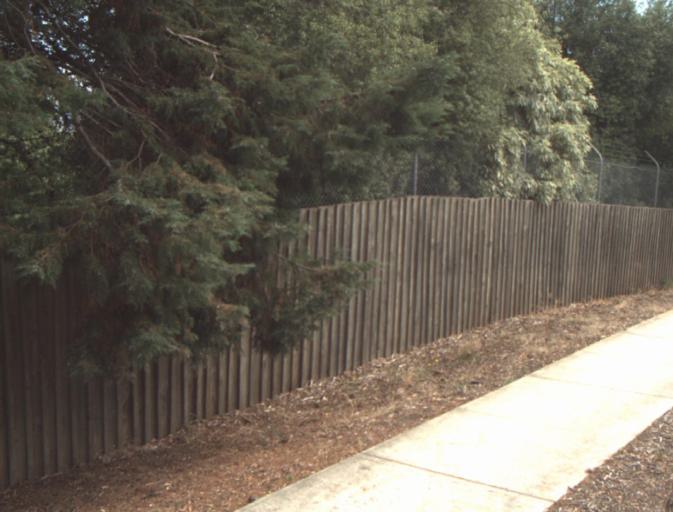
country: AU
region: Tasmania
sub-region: Launceston
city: West Launceston
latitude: -41.4528
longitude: 147.1204
